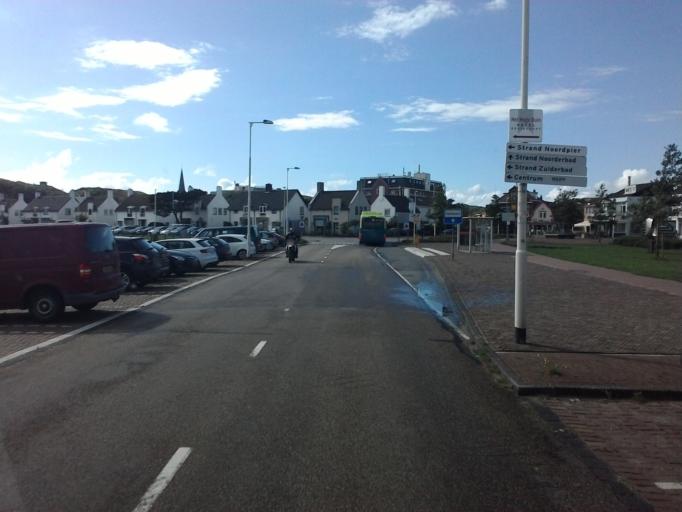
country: NL
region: North Holland
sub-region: Gemeente Beverwijk
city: Beverwijk
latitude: 52.4935
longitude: 4.5953
